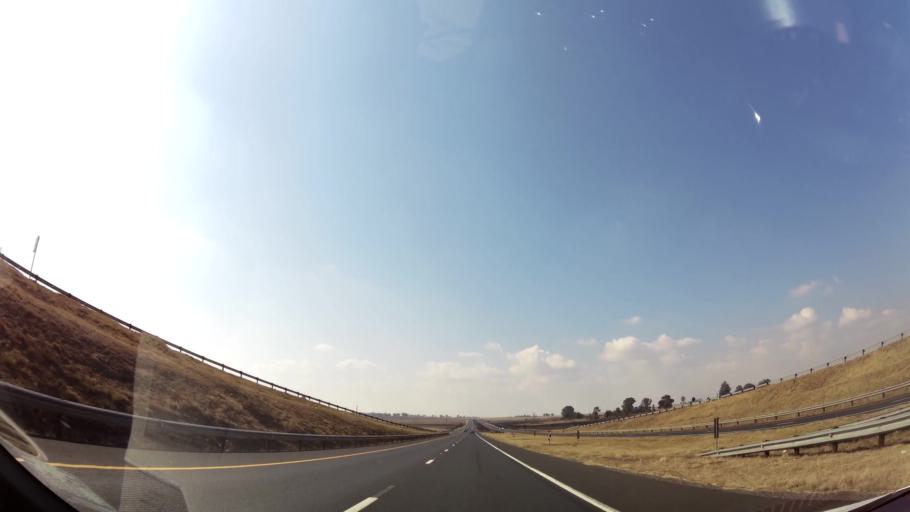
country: ZA
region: Gauteng
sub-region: Ekurhuleni Metropolitan Municipality
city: Springs
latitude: -26.1639
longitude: 28.4950
